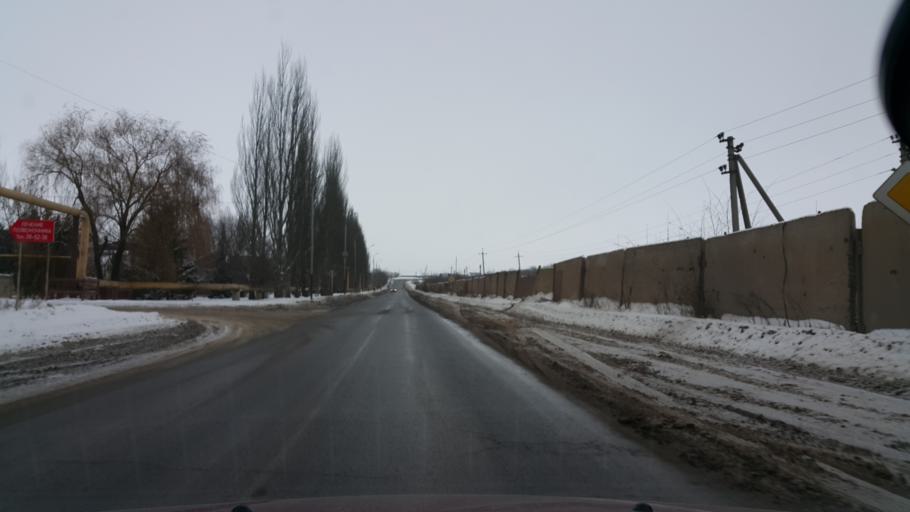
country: RU
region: Tambov
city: Pokrovo-Prigorodnoye
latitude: 52.6599
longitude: 41.4176
